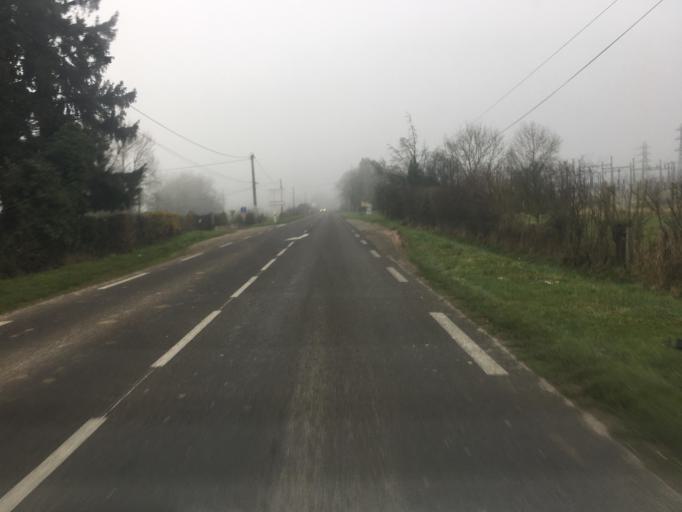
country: FR
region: Haute-Normandie
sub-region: Departement de la Seine-Maritime
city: Neufchatel-en-Bray
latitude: 49.7257
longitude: 1.4257
